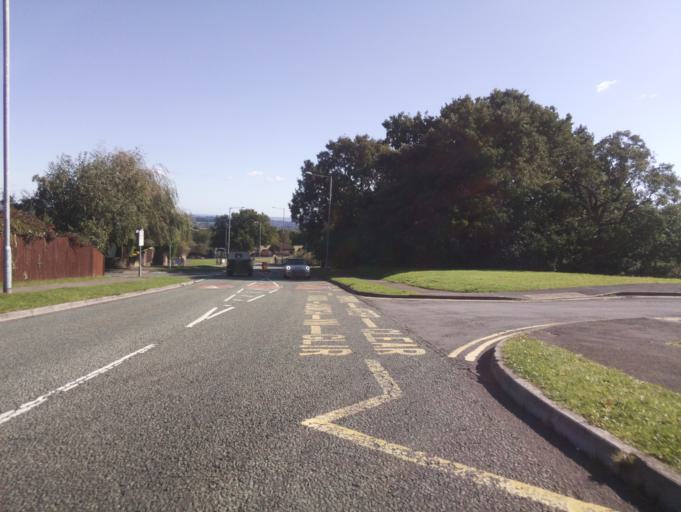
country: GB
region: Wales
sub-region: Torfaen County Borough
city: Cwmbran
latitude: 51.6432
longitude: -3.0581
